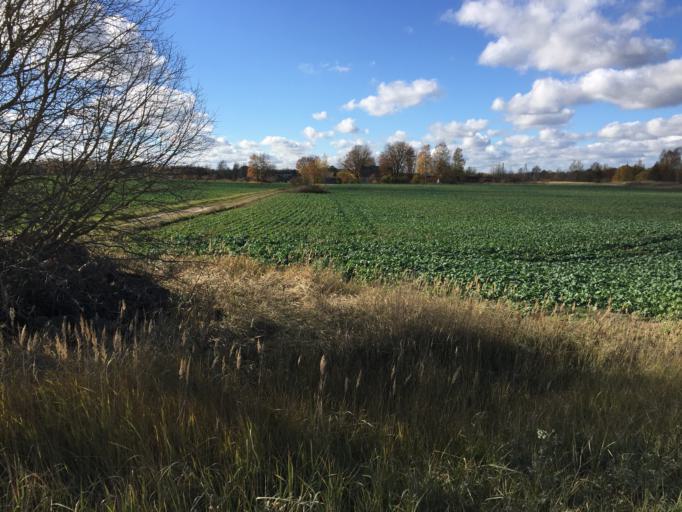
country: LV
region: Tukuma Rajons
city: Tukums
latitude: 56.9668
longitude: 22.9658
